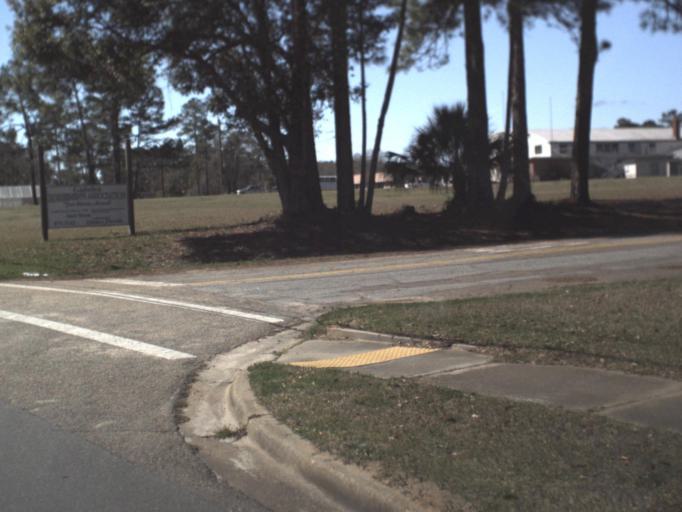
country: US
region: Florida
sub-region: Gadsden County
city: Quincy
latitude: 30.5849
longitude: -84.6069
